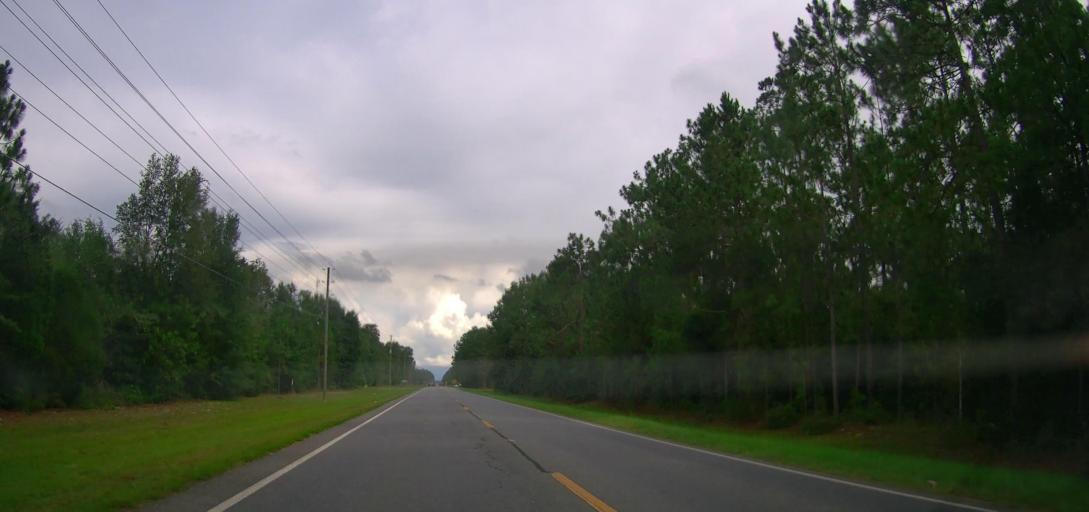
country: US
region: Georgia
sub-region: Wayne County
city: Jesup
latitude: 31.6479
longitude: -81.9087
